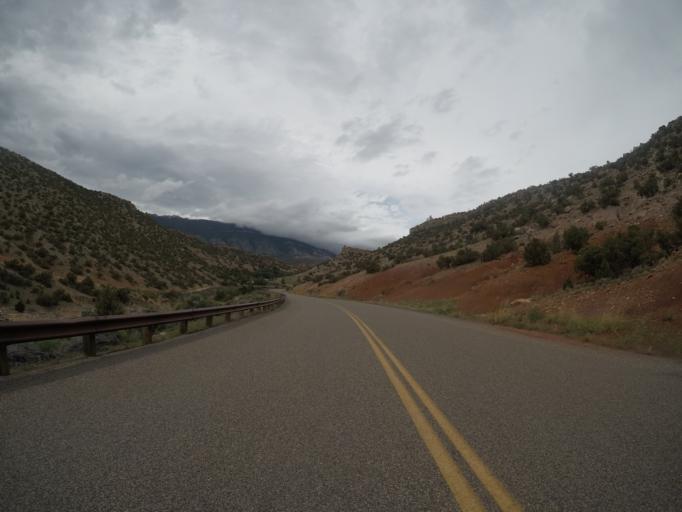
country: US
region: Wyoming
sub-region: Big Horn County
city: Lovell
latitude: 45.1007
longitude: -108.2189
